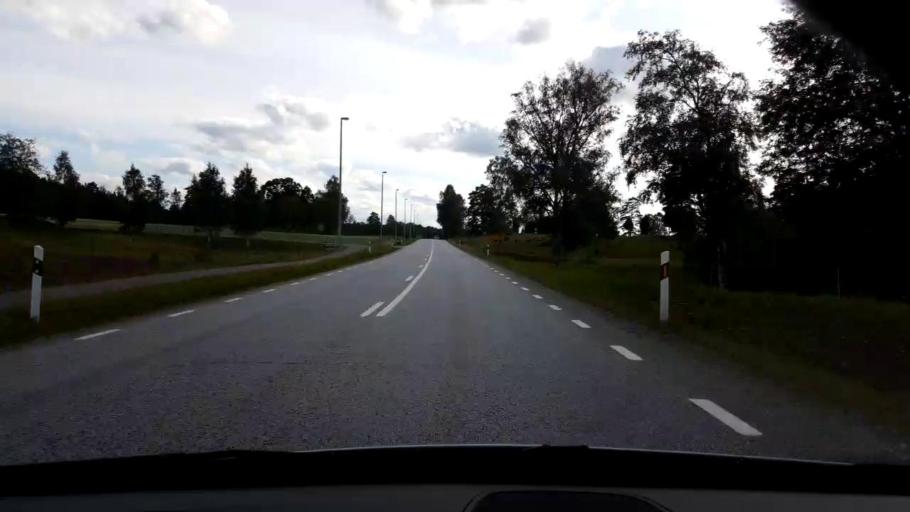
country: SE
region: Joenkoeping
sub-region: Savsjo Kommun
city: Vrigstad
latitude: 57.3641
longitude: 14.4946
